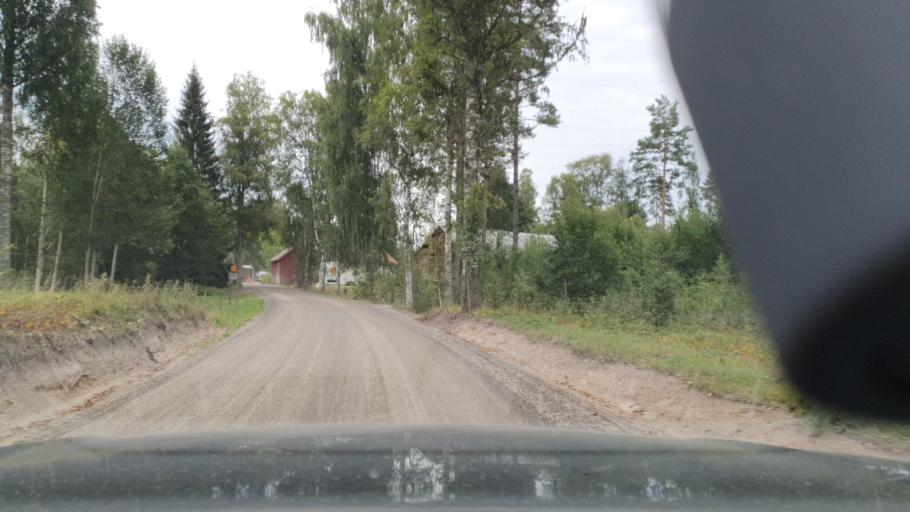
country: SE
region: Vaermland
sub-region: Torsby Kommun
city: Torsby
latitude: 59.9461
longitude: 12.9018
